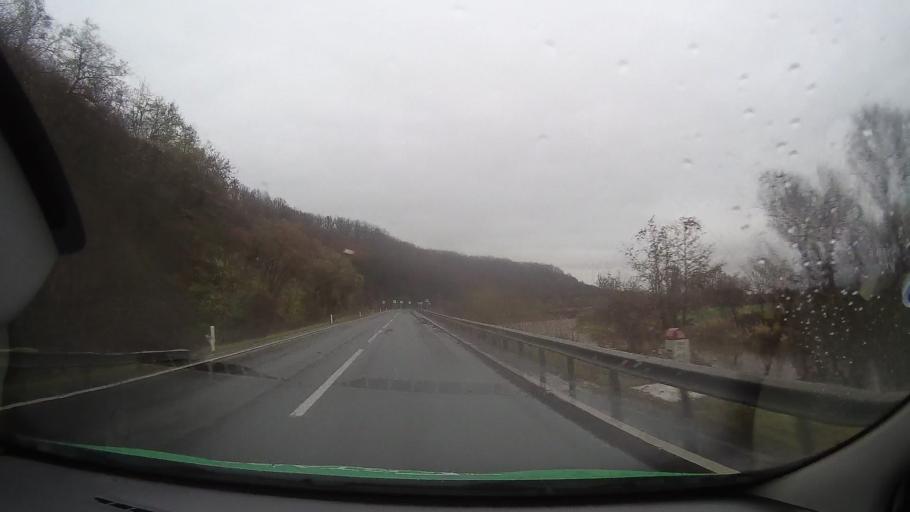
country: RO
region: Mures
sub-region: Comuna Brancovenesti
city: Brancovenesti
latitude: 46.8647
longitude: 24.7684
